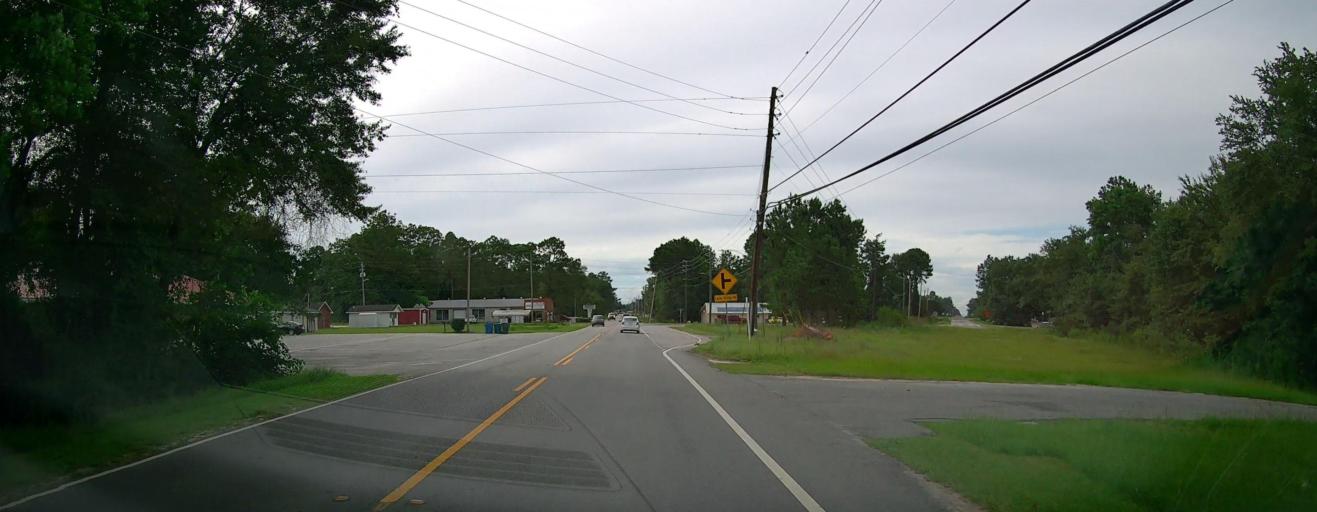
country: US
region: Georgia
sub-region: Wayne County
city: Jesup
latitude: 31.6142
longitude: -81.8938
